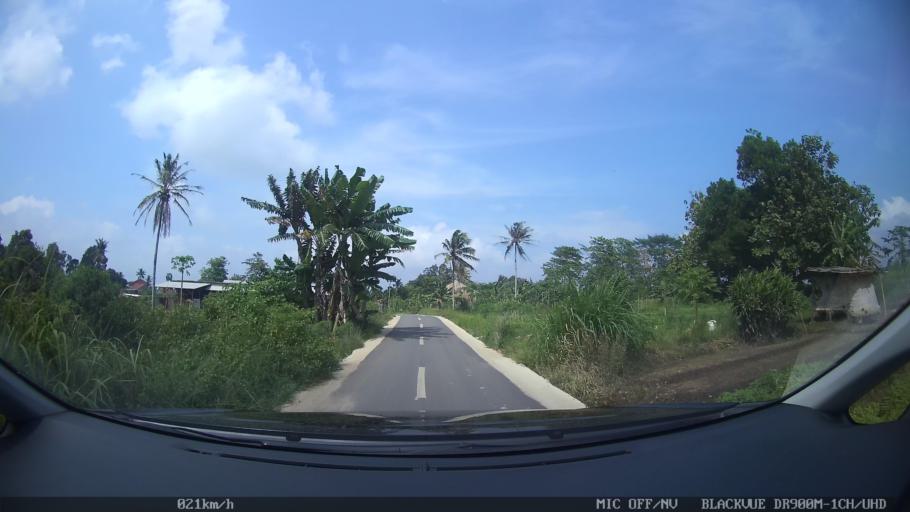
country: ID
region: Lampung
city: Kedaton
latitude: -5.3371
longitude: 105.2732
